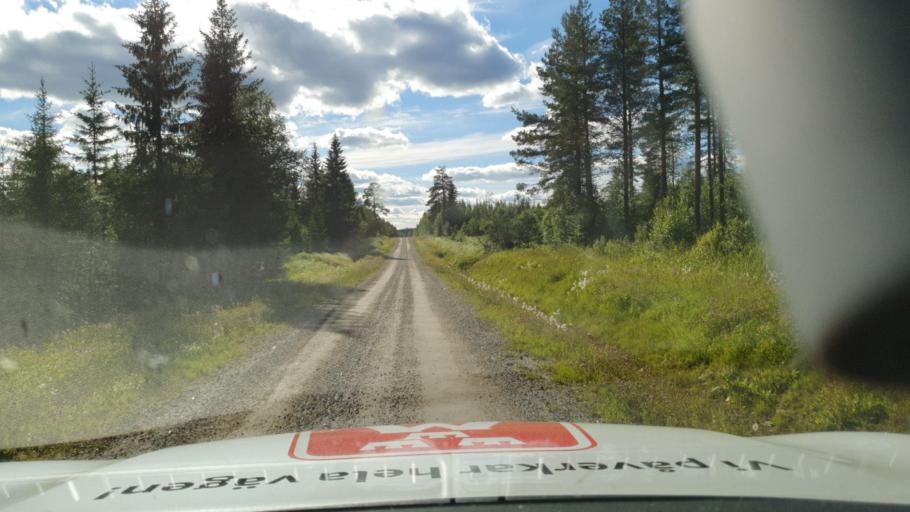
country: SE
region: Vaesterbotten
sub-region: Lycksele Kommun
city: Lycksele
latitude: 64.4011
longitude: 18.3318
